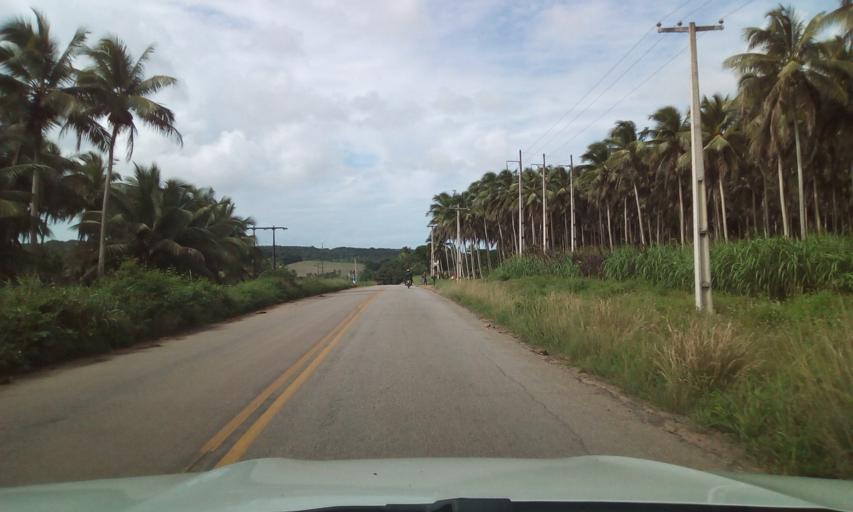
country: BR
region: Paraiba
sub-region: Cabedelo
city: Cabedelo
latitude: -6.9474
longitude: -34.9331
